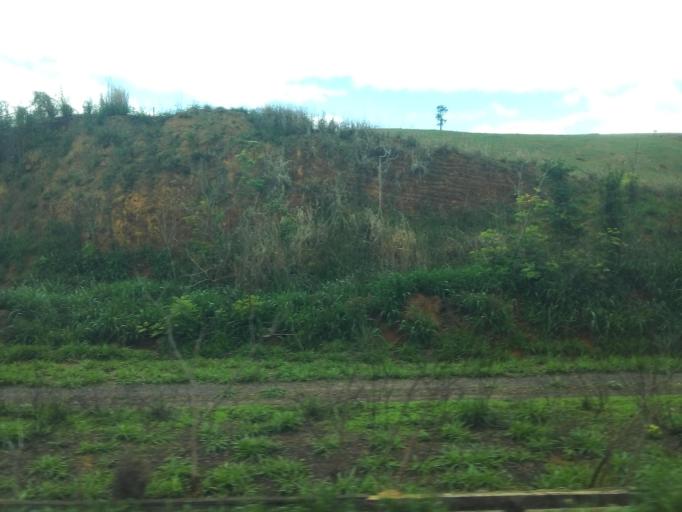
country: BR
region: Minas Gerais
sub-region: Governador Valadares
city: Governador Valadares
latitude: -19.0750
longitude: -42.1556
